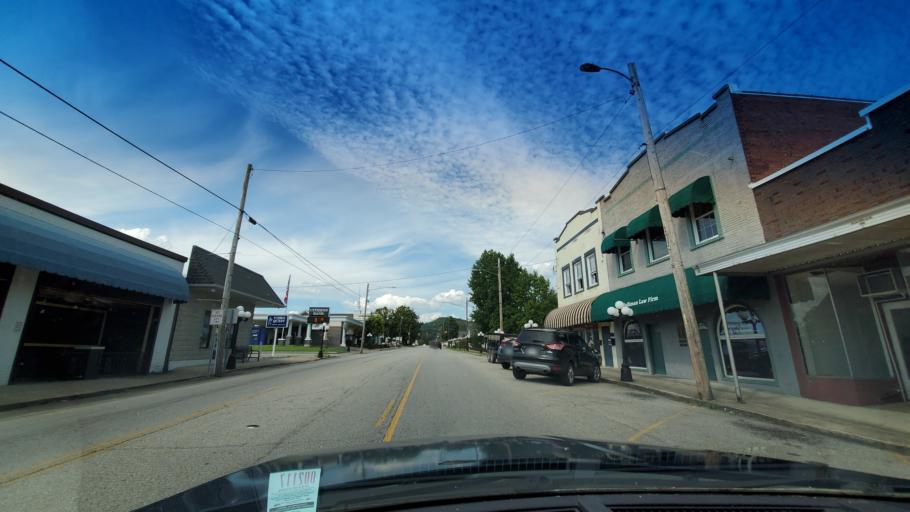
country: US
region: Tennessee
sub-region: Smith County
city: Carthage
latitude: 36.2527
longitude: -85.9519
